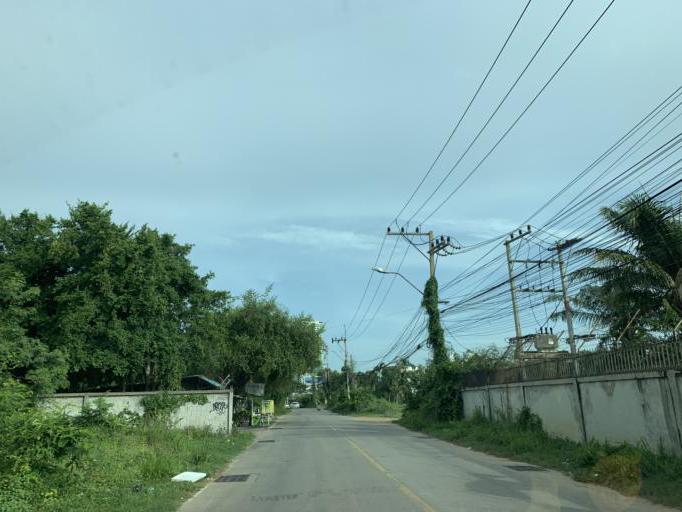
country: TH
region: Chon Buri
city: Phatthaya
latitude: 12.9008
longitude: 100.8754
